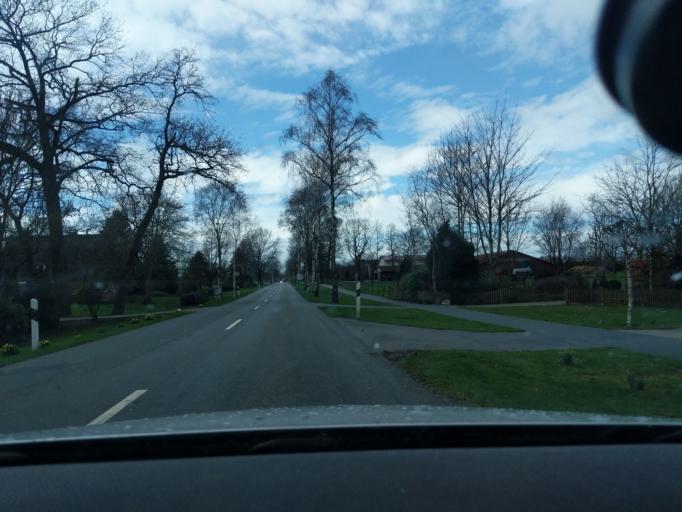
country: DE
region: Lower Saxony
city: Drochtersen
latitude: 53.6666
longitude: 9.3906
